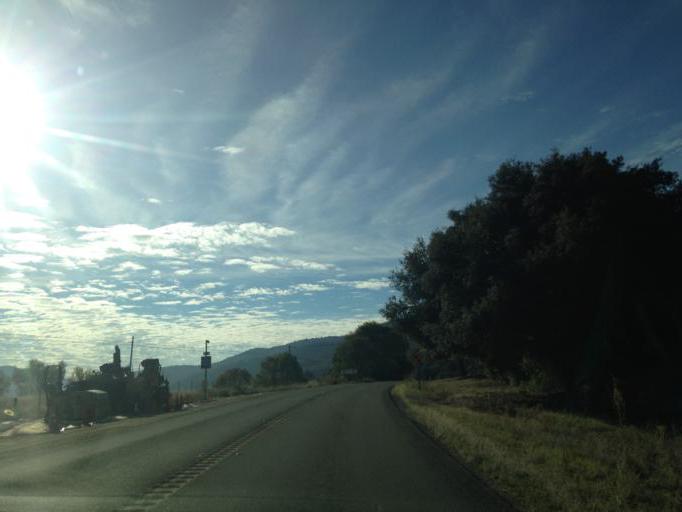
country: US
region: California
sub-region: San Diego County
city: Ramona
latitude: 33.2342
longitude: -116.7601
